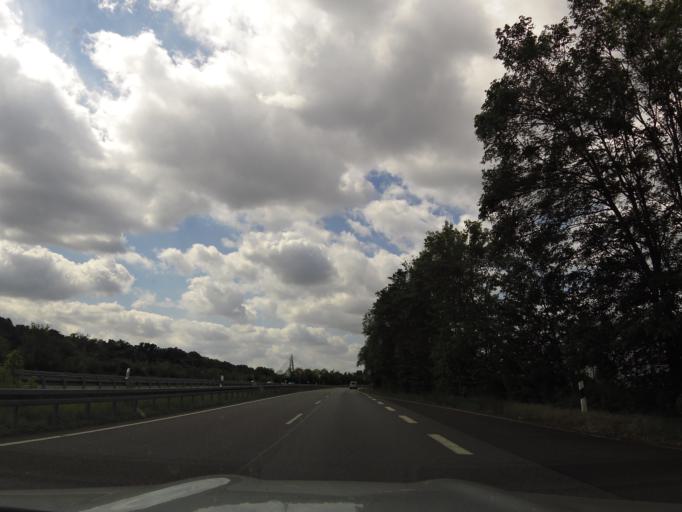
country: DE
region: Hesse
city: Raunheim
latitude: 50.0236
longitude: 8.4723
